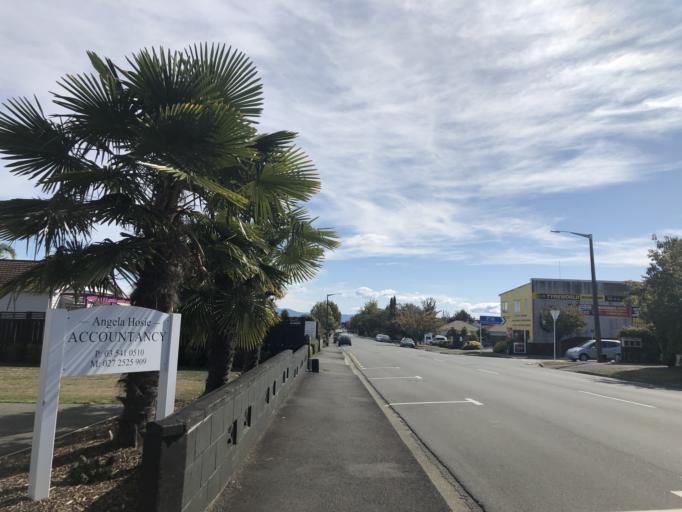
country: NZ
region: Tasman
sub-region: Tasman District
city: Richmond
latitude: -41.3415
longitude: 173.1847
